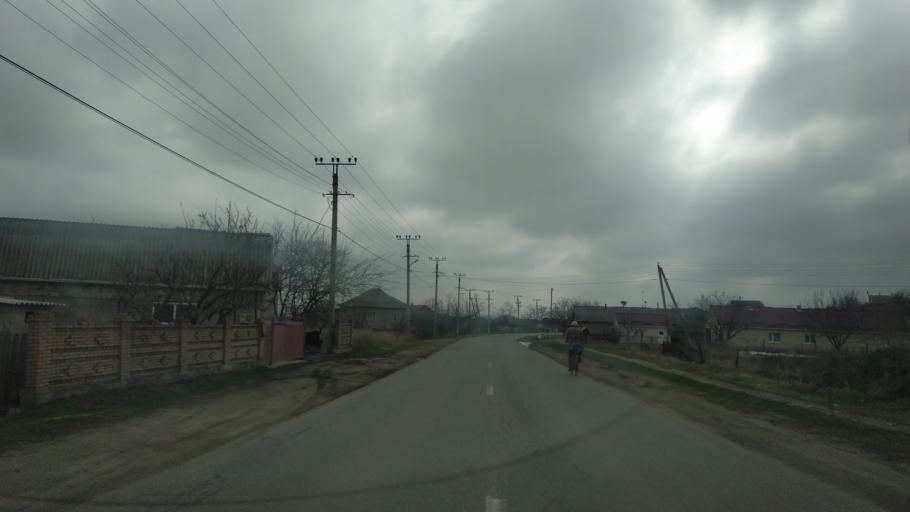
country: MD
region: Cimislia
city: Cimislia
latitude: 46.5183
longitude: 28.7941
